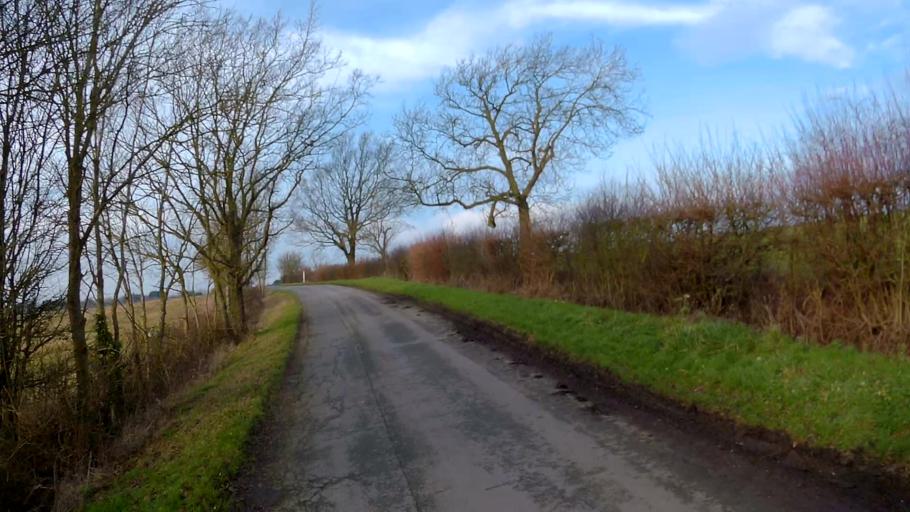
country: GB
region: England
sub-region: Lincolnshire
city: Bourne
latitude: 52.7383
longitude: -0.4007
